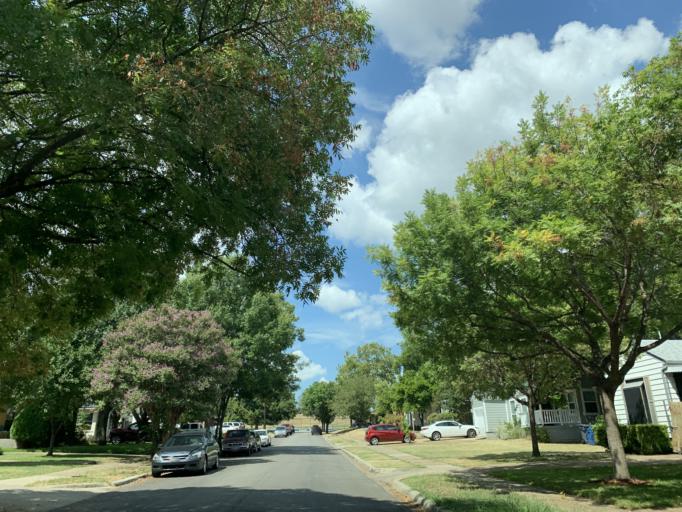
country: US
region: Texas
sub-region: Dallas County
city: Cockrell Hill
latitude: 32.7432
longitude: -96.8595
